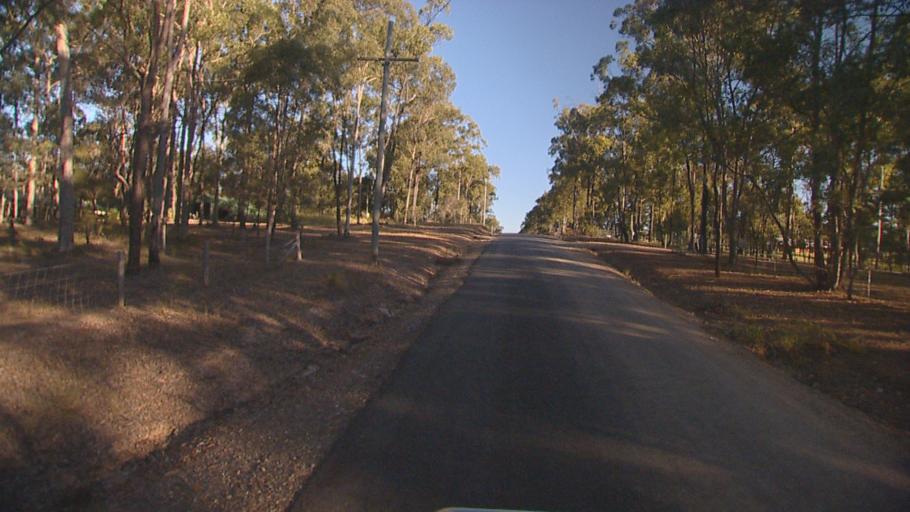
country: AU
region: Queensland
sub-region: Logan
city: Chambers Flat
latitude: -27.7641
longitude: 153.1333
